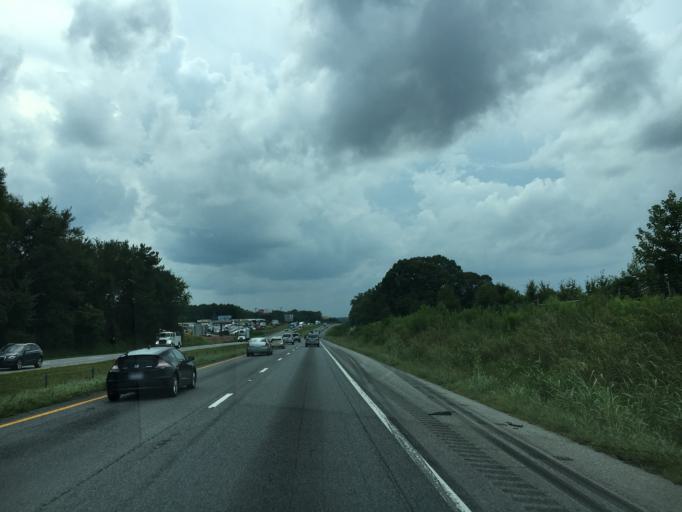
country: US
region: South Carolina
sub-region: Spartanburg County
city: Cowpens
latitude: 35.0388
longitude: -81.8298
